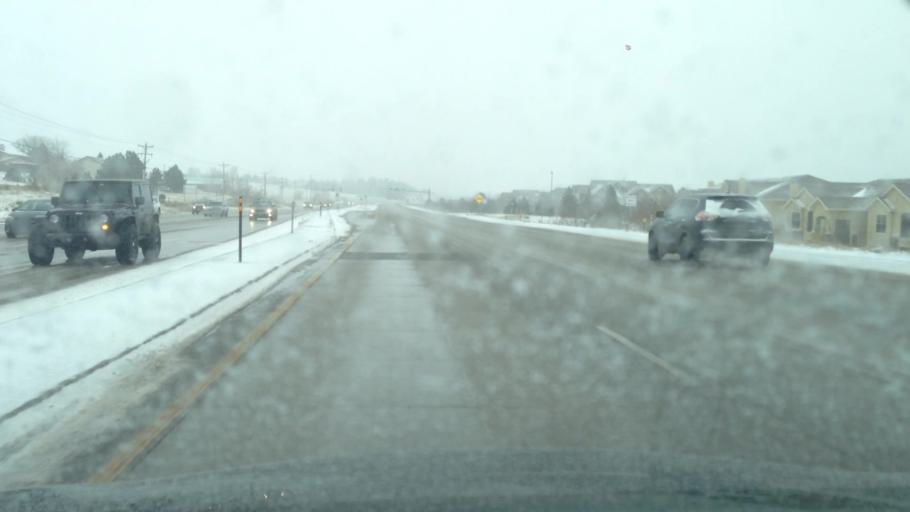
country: US
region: Colorado
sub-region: Arapahoe County
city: Dove Valley
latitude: 39.5873
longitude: -104.7978
